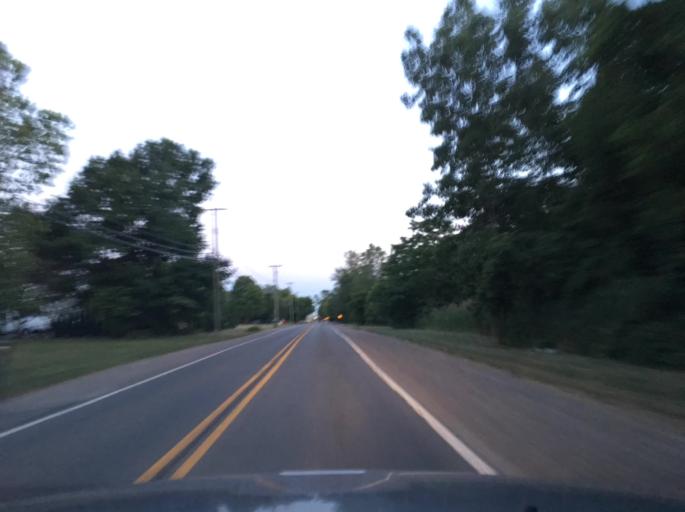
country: US
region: Michigan
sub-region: Macomb County
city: Mount Clemens
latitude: 42.6232
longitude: -82.8883
